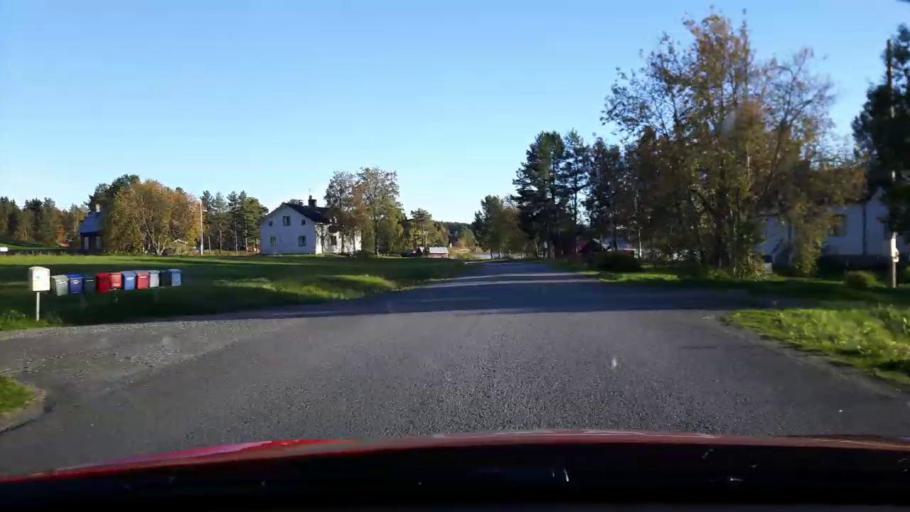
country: SE
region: Jaemtland
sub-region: OEstersunds Kommun
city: Lit
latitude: 63.6128
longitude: 14.7715
